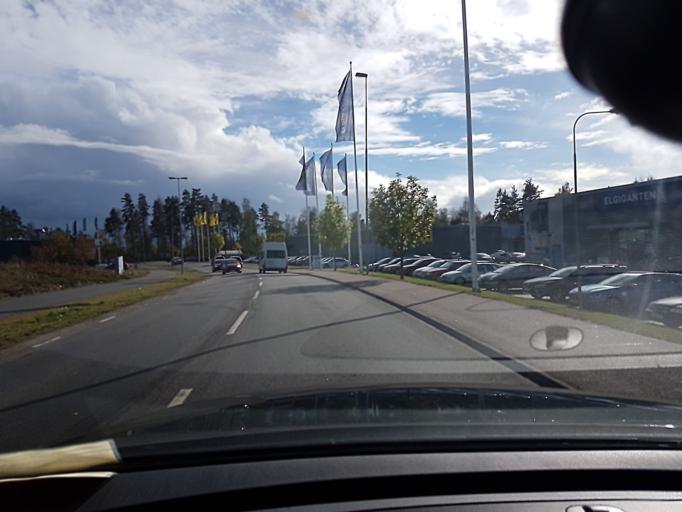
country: SE
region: Kronoberg
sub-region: Vaxjo Kommun
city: Vaexjoe
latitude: 56.8822
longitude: 14.7633
